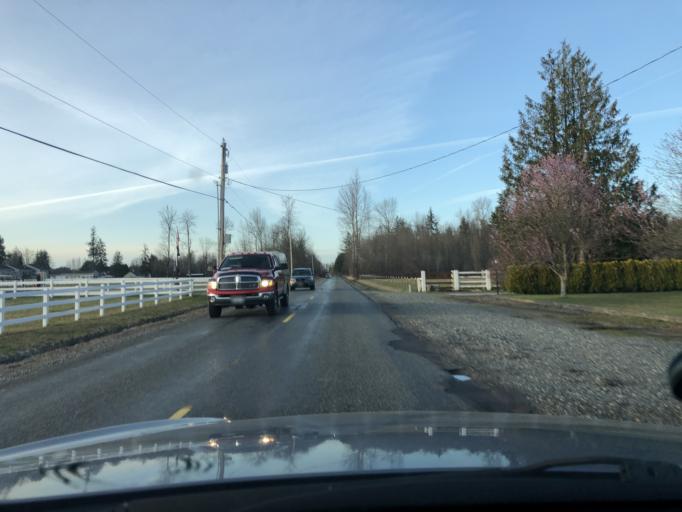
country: US
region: Washington
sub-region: Pierce County
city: Bonney Lake
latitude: 47.2160
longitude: -122.1228
